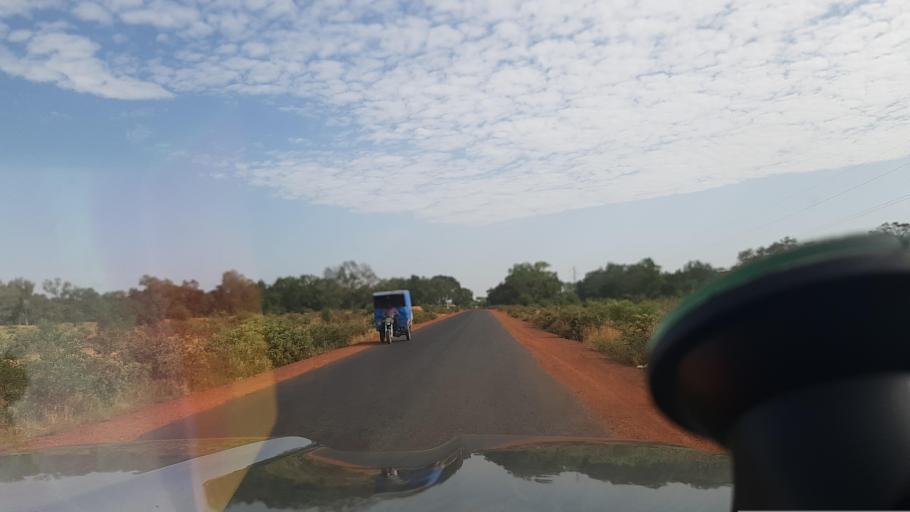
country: ML
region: Segou
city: Segou
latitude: 13.5263
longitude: -6.1305
